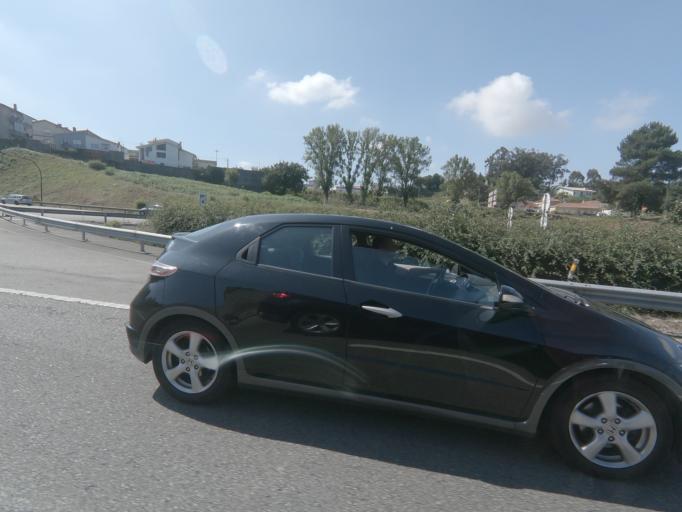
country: PT
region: Porto
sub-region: Maia
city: Pedroucos
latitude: 41.1993
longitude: -8.5800
